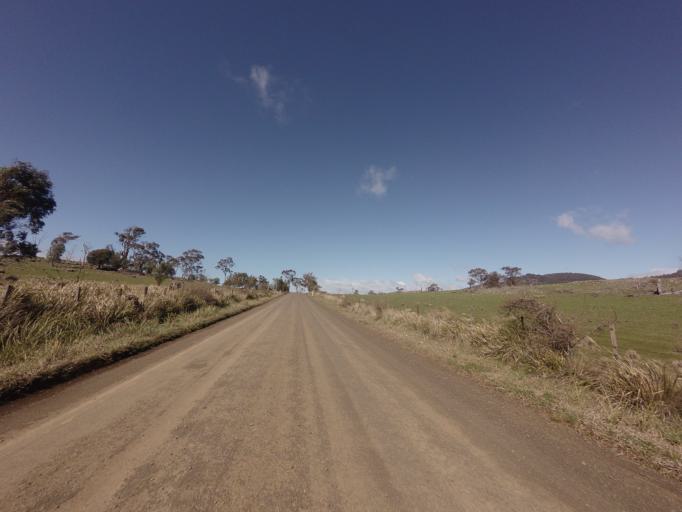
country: AU
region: Tasmania
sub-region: Northern Midlands
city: Evandale
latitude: -41.9389
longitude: 147.4226
